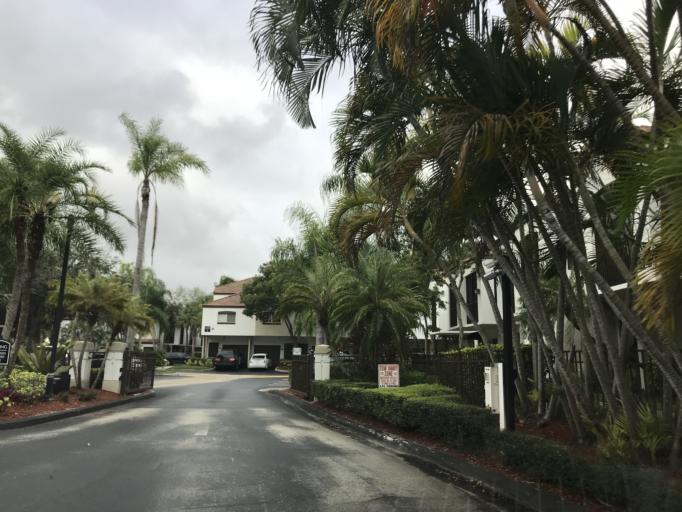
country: US
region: Florida
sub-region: Broward County
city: Coral Springs
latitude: 26.2990
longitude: -80.2807
